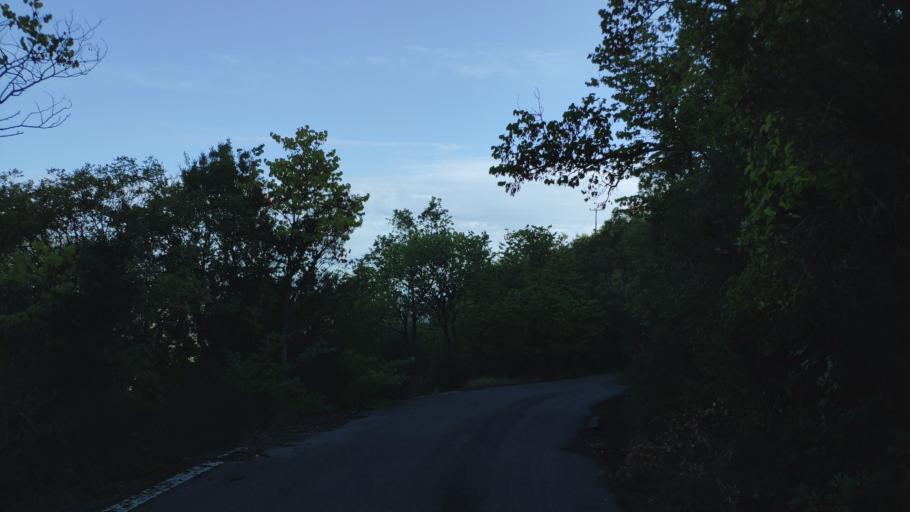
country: GR
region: Peloponnese
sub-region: Nomos Arkadias
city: Dimitsana
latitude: 37.5578
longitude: 22.0401
